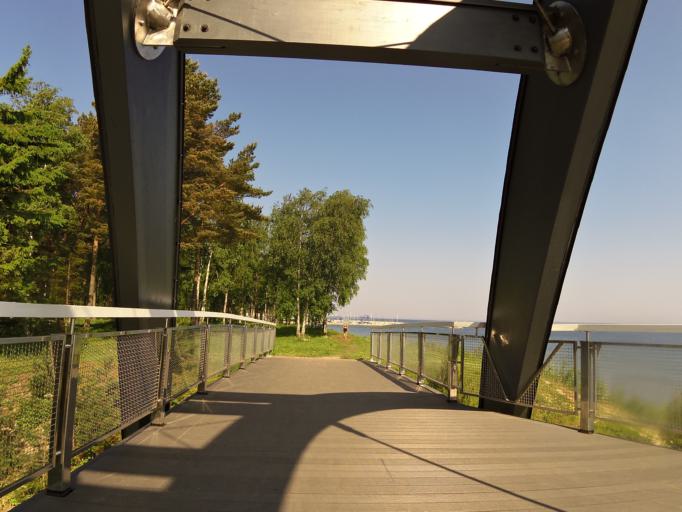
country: EE
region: Harju
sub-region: Harku vald
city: Tabasalu
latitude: 59.4464
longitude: 24.6152
